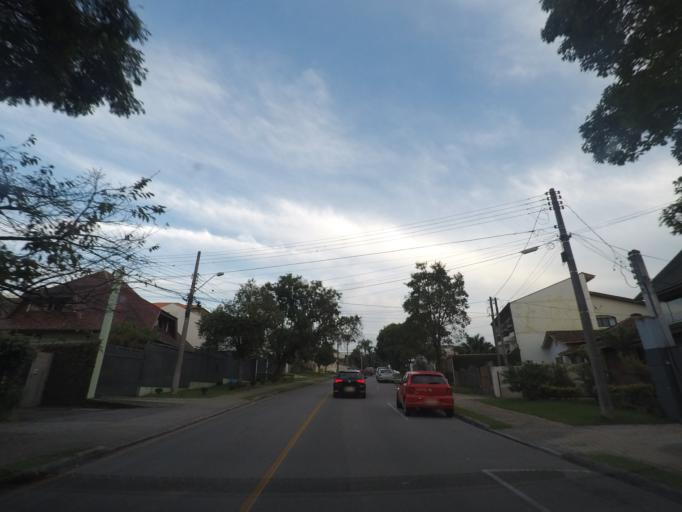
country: BR
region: Parana
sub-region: Curitiba
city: Curitiba
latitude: -25.4164
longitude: -49.2757
